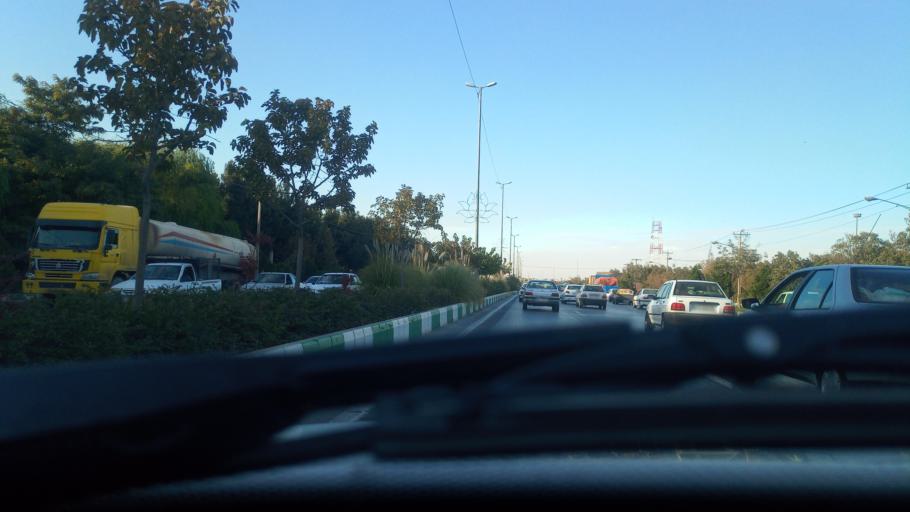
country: IR
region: Razavi Khorasan
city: Mashhad
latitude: 36.2282
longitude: 59.6254
